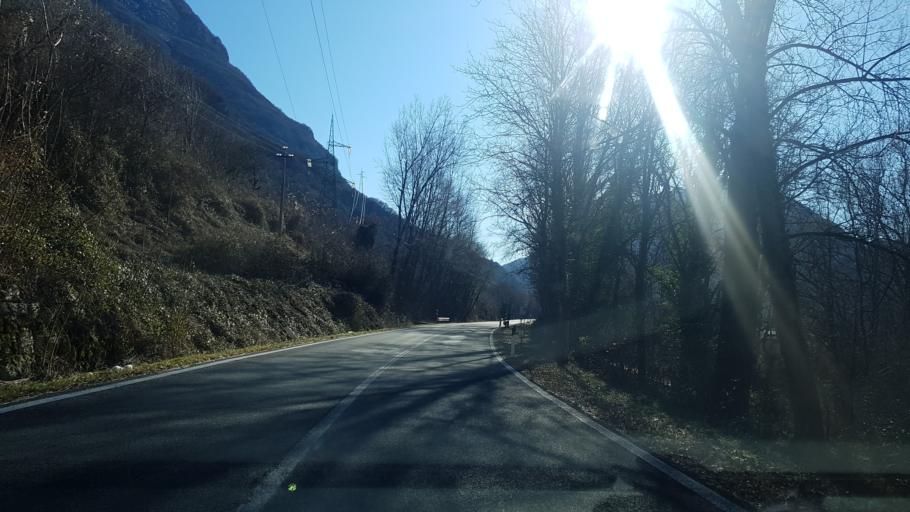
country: IT
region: Friuli Venezia Giulia
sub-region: Provincia di Udine
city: Amaro
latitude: 46.3439
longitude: 13.0743
